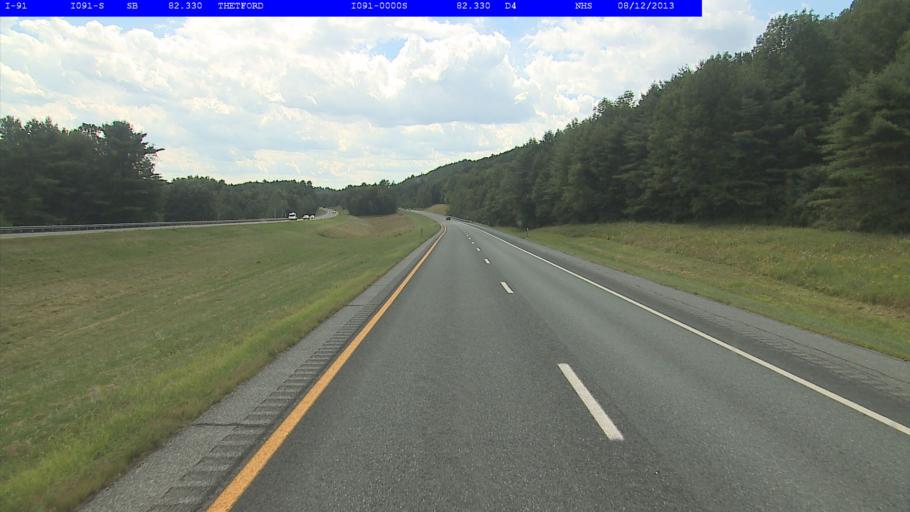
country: US
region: New Hampshire
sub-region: Grafton County
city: Lyme
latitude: 43.7871
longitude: -72.2164
